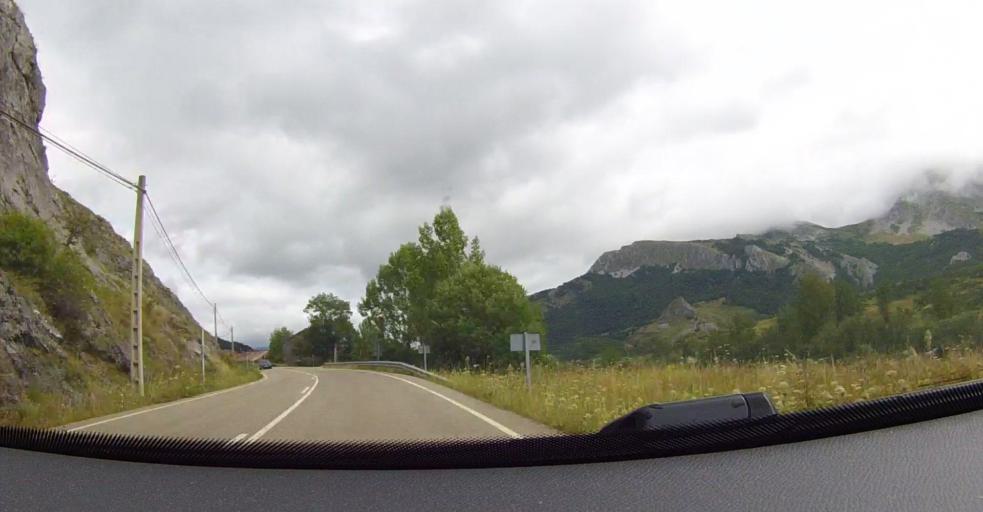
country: ES
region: Castille and Leon
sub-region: Provincia de Leon
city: Buron
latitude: 43.0260
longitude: -5.0565
